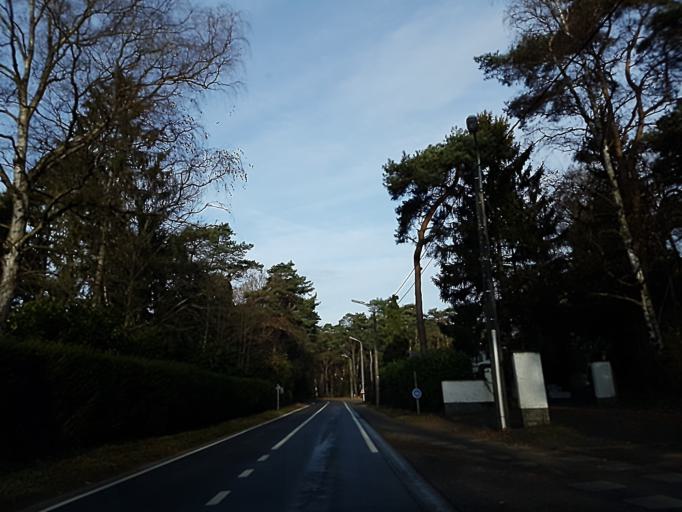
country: BE
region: Flanders
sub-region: Provincie Vlaams-Brabant
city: Keerbergen
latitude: 50.9968
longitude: 4.6470
